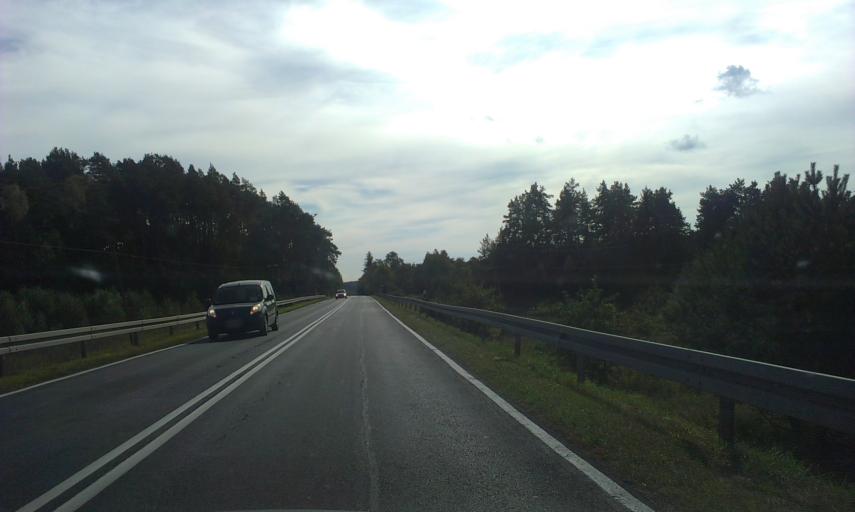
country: PL
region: Greater Poland Voivodeship
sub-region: Powiat zlotowski
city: Okonek
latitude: 53.5449
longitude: 16.8432
